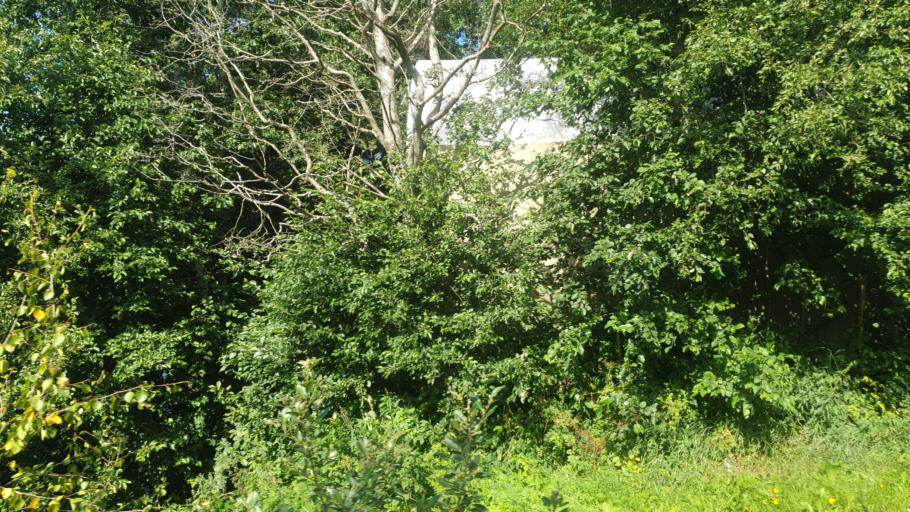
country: NO
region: Sor-Trondelag
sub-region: Orkdal
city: Orkanger
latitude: 63.2843
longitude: 9.8385
